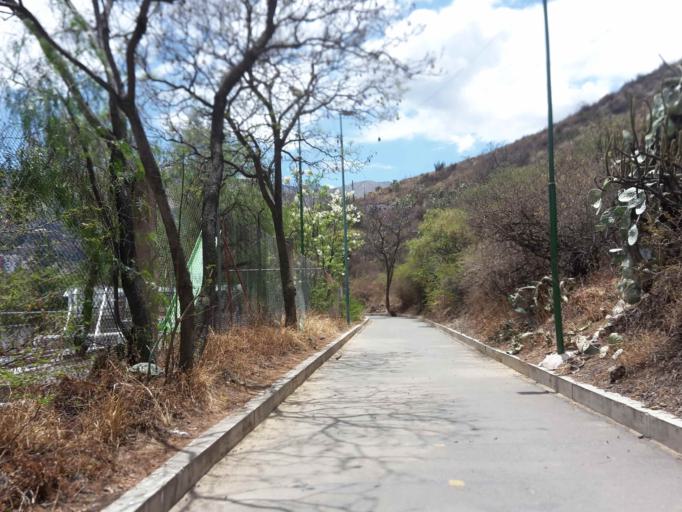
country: BO
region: Cochabamba
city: Cochabamba
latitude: -17.3800
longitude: -66.1390
